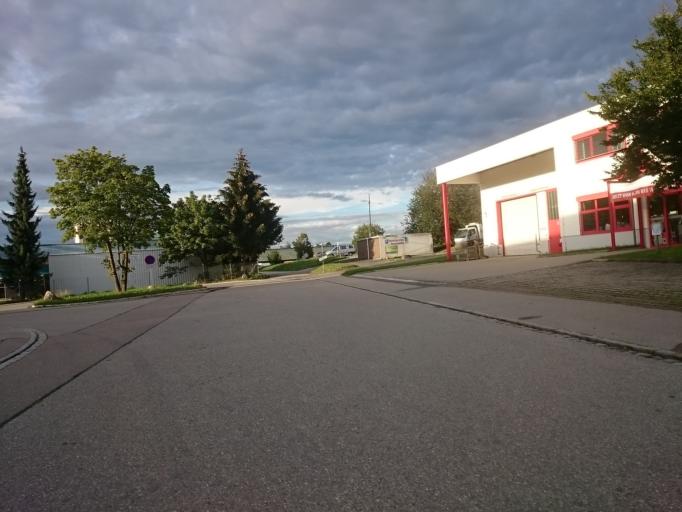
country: DE
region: Bavaria
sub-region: Swabia
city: Kempten (Allgaeu)
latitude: 47.7554
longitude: 10.3193
